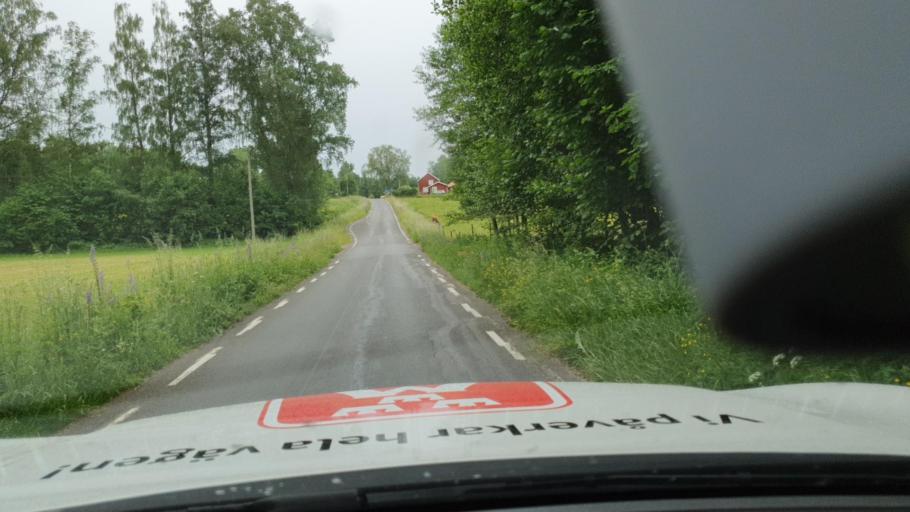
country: SE
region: Vaestra Goetaland
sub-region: Hjo Kommun
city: Hjo
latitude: 58.3151
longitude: 14.1838
